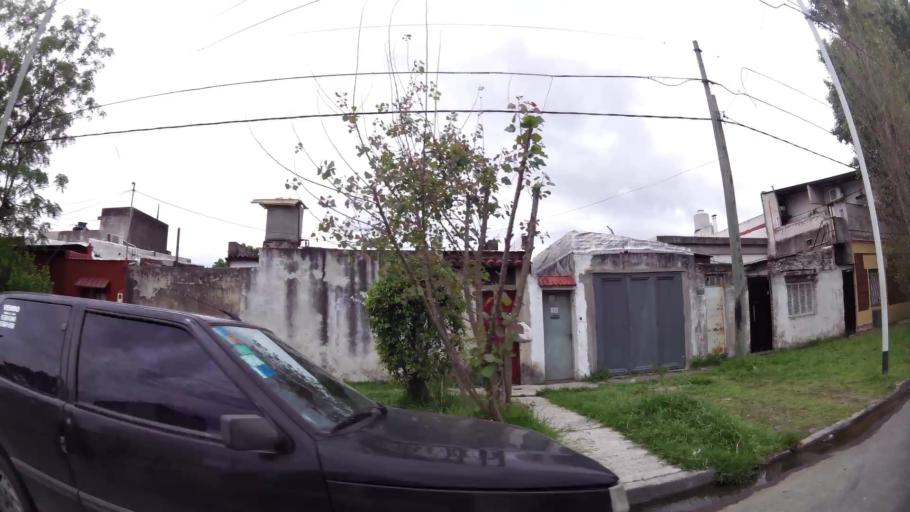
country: AR
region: Buenos Aires
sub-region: Partido de Avellaneda
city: Avellaneda
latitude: -34.6784
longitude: -58.3774
